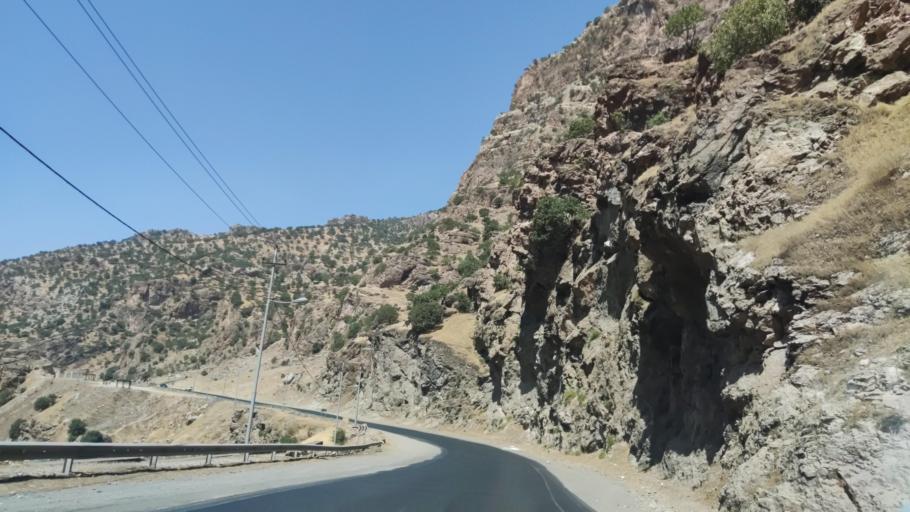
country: IQ
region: Arbil
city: Ruwandiz
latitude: 36.6310
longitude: 44.4811
